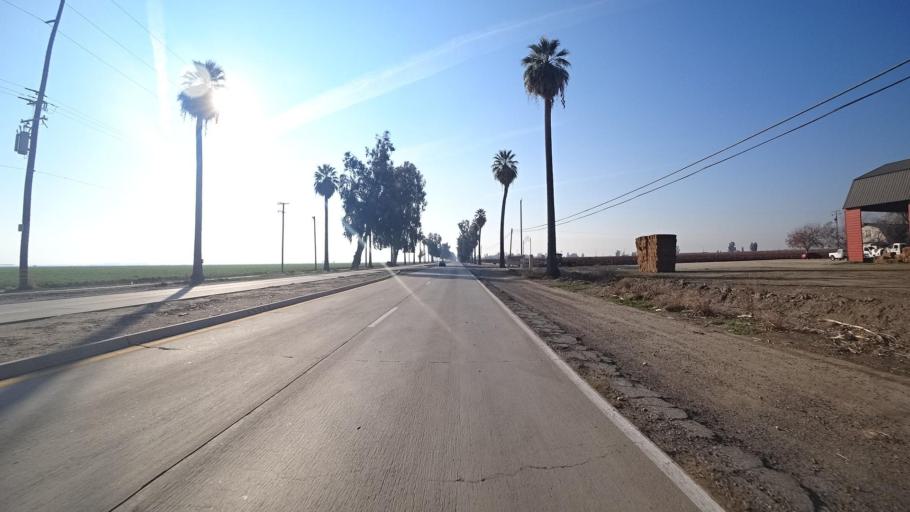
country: US
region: California
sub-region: Kern County
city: Greenfield
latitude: 35.2167
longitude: -119.0032
